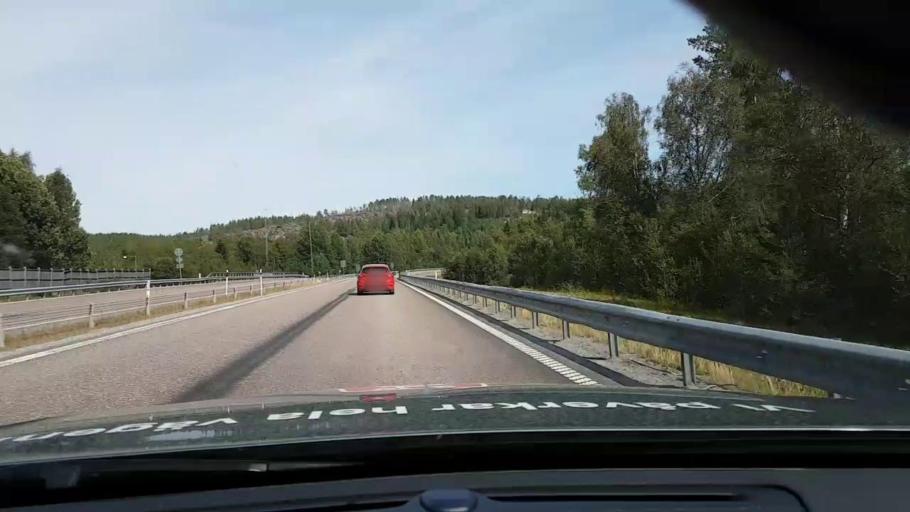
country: SE
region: Vaesternorrland
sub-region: OErnskoeldsviks Kommun
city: Ornskoldsvik
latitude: 63.3140
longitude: 18.7925
